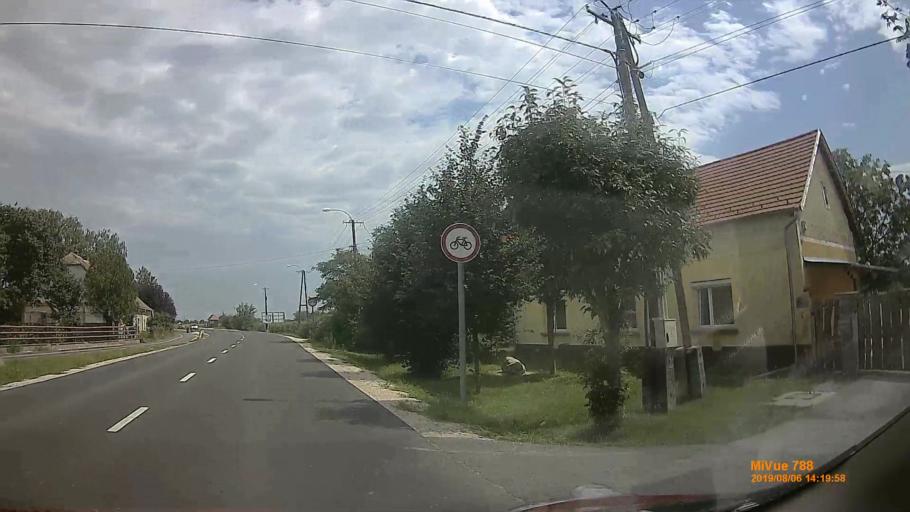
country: HU
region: Vas
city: Taplanszentkereszt
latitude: 47.1790
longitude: 16.7531
